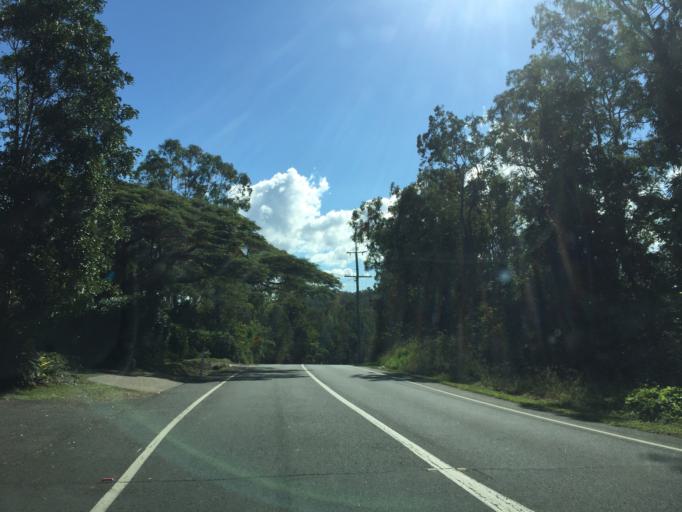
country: AU
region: Queensland
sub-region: Brisbane
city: Kenmore Hills
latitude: -27.4924
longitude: 152.9253
